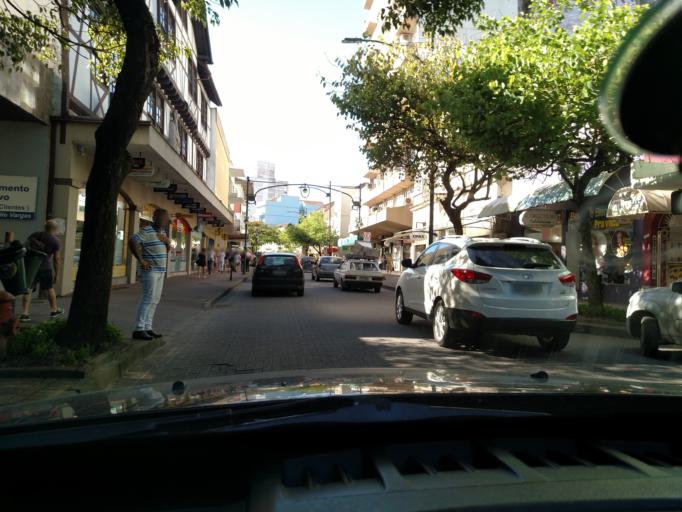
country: BR
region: Santa Catarina
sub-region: Blumenau
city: Blumenau
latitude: -26.9171
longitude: -49.0680
